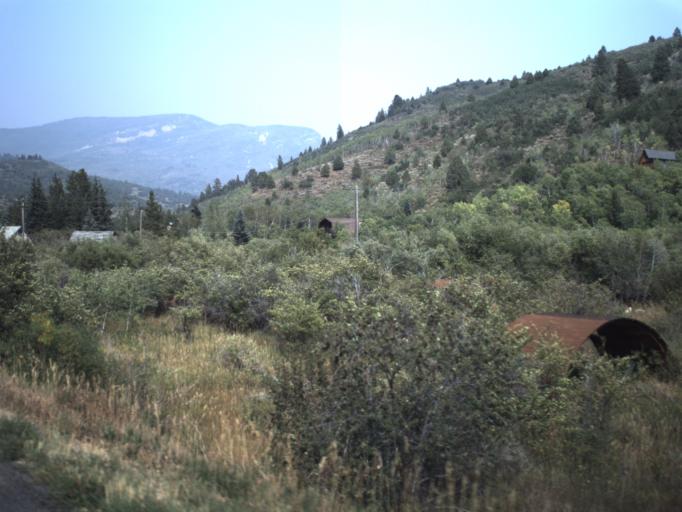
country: US
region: Utah
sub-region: Summit County
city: Francis
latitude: 40.6209
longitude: -111.2056
